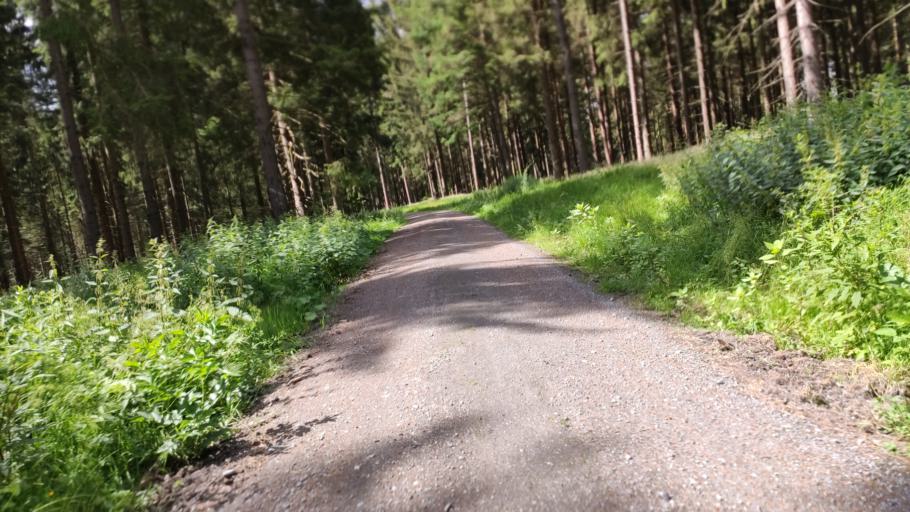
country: DE
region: Bavaria
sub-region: Upper Franconia
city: Tschirn
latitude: 50.4084
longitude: 11.4715
